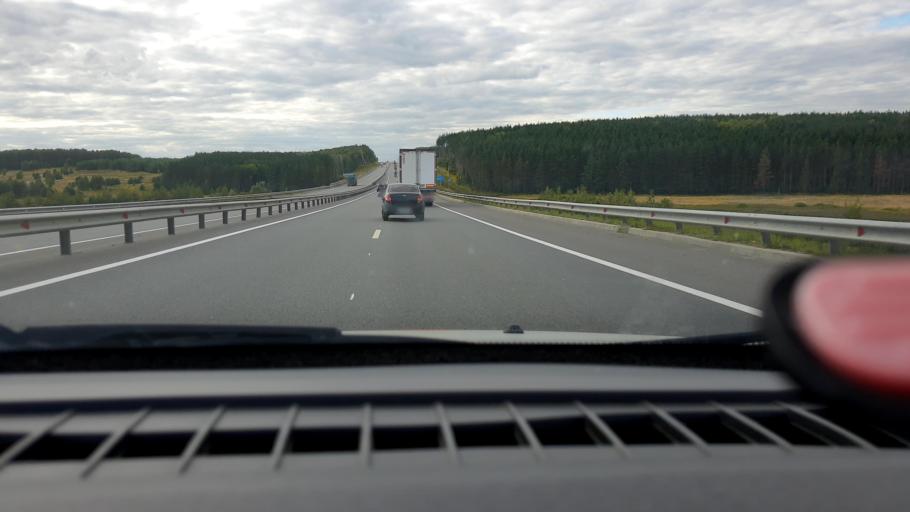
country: RU
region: Nizjnij Novgorod
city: Kstovo
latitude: 56.0759
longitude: 44.1046
